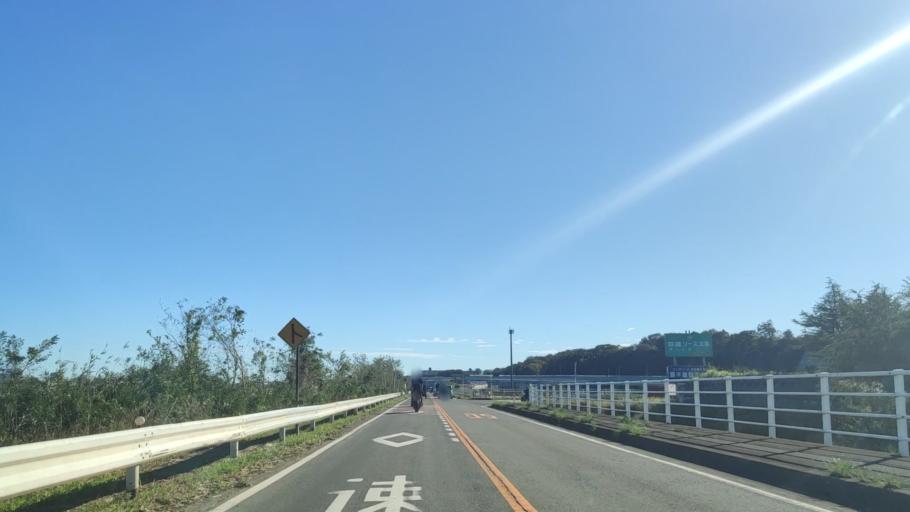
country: JP
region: Kanagawa
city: Zama
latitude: 35.4980
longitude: 139.3709
